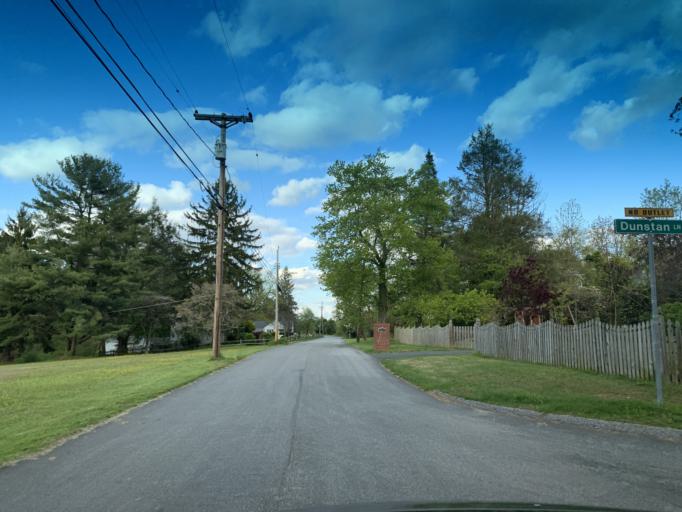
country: US
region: Maryland
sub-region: Harford County
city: Jarrettsville
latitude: 39.5328
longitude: -76.5388
